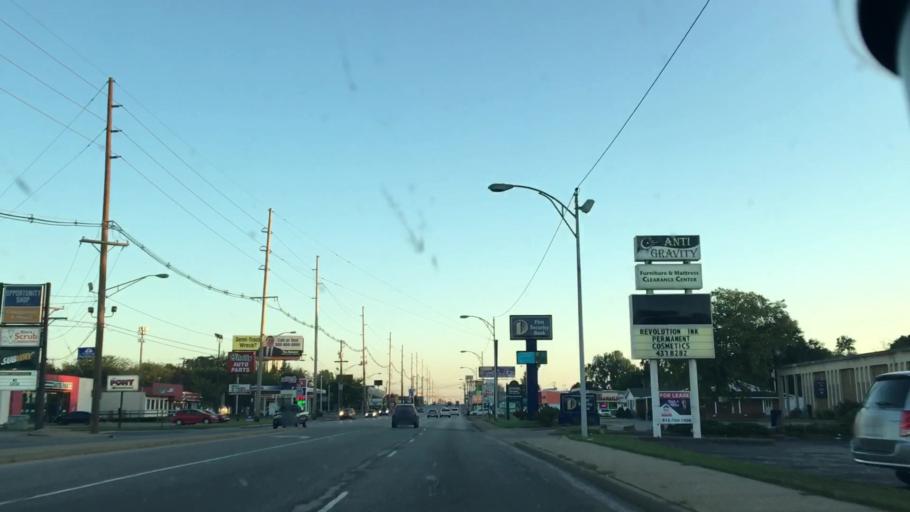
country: US
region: Indiana
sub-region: Vanderburgh County
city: Melody Hill
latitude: 37.9752
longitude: -87.4927
